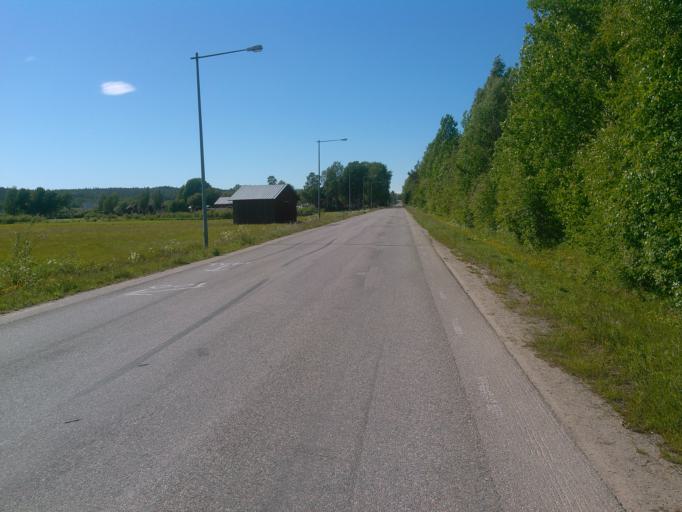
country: SE
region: Vaesterbotten
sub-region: Umea Kommun
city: Roback
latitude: 63.8205
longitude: 20.1951
